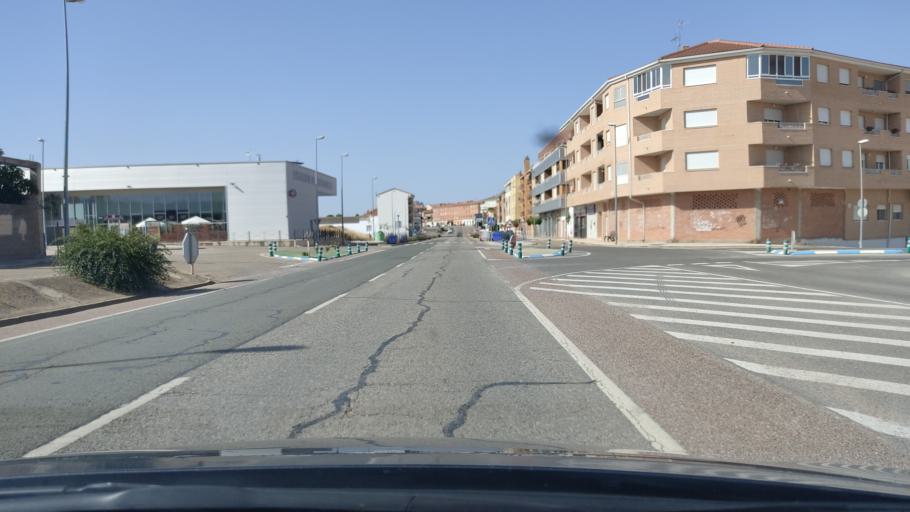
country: ES
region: Aragon
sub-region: Provincia de Teruel
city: Calamocha
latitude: 40.9150
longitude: -1.2969
